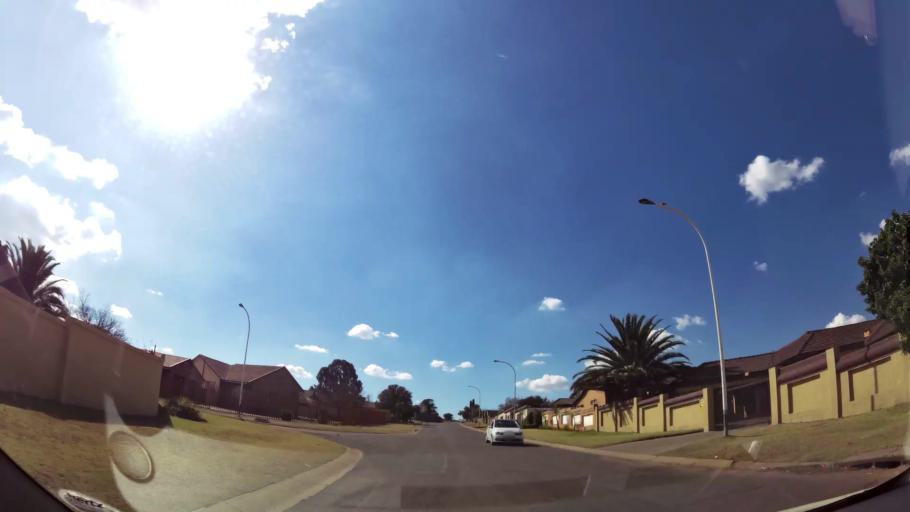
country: ZA
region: Mpumalanga
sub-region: Nkangala District Municipality
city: Witbank
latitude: -25.9308
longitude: 29.2470
